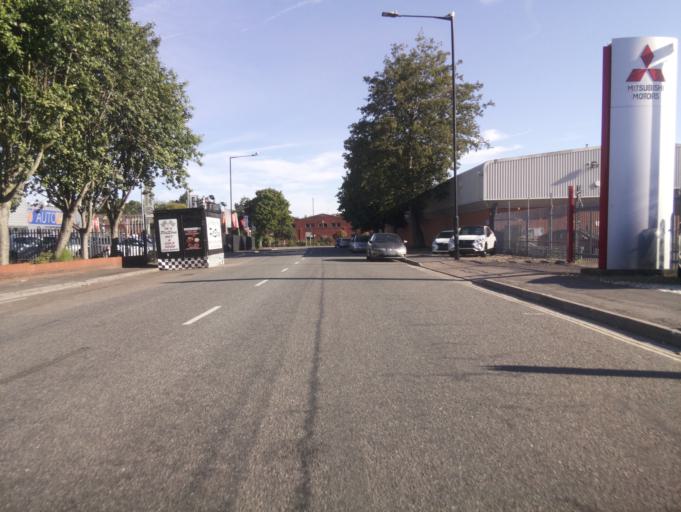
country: GB
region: England
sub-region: Bristol
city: Bristol
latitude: 51.4489
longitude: -2.5703
